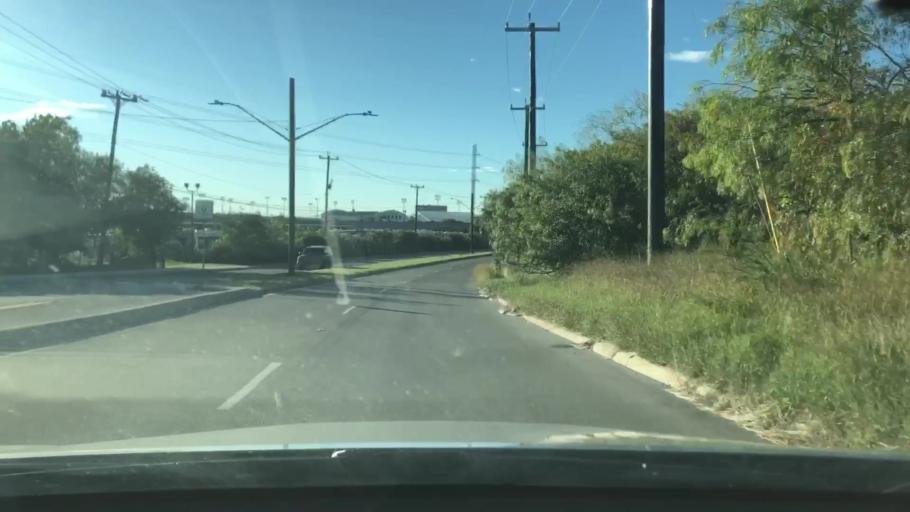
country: US
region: Texas
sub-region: Bexar County
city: Hollywood Park
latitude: 29.5470
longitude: -98.4594
